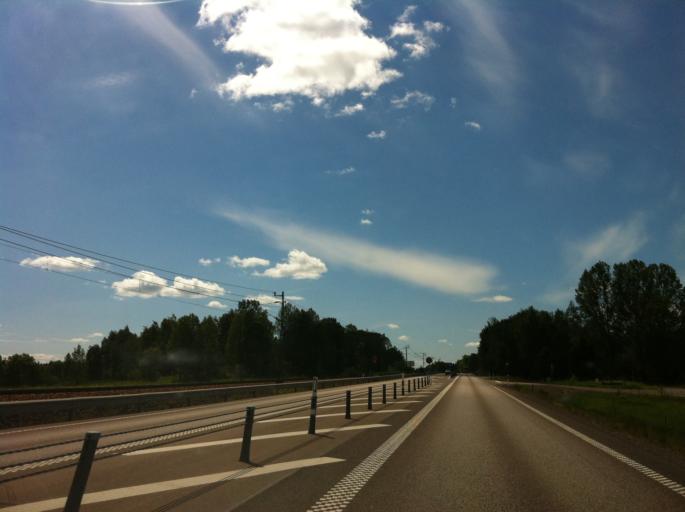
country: SE
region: Vaestra Goetaland
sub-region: Melleruds Kommun
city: Mellerud
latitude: 58.8649
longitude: 12.5615
